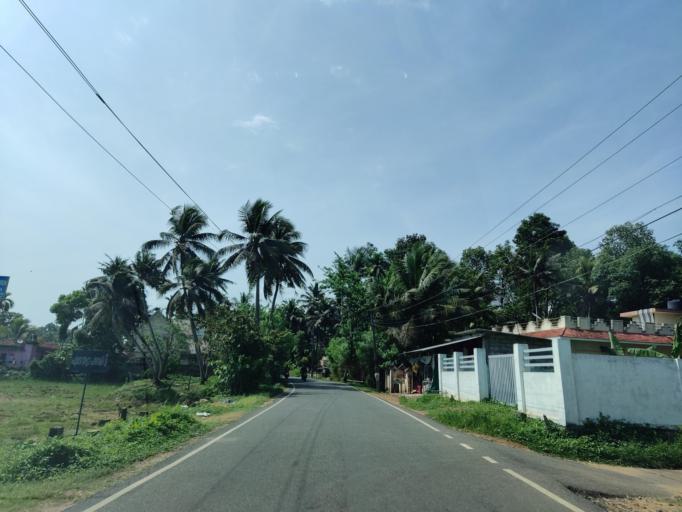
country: IN
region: Kerala
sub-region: Pattanamtitta
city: Tiruvalla
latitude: 9.3519
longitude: 76.4695
